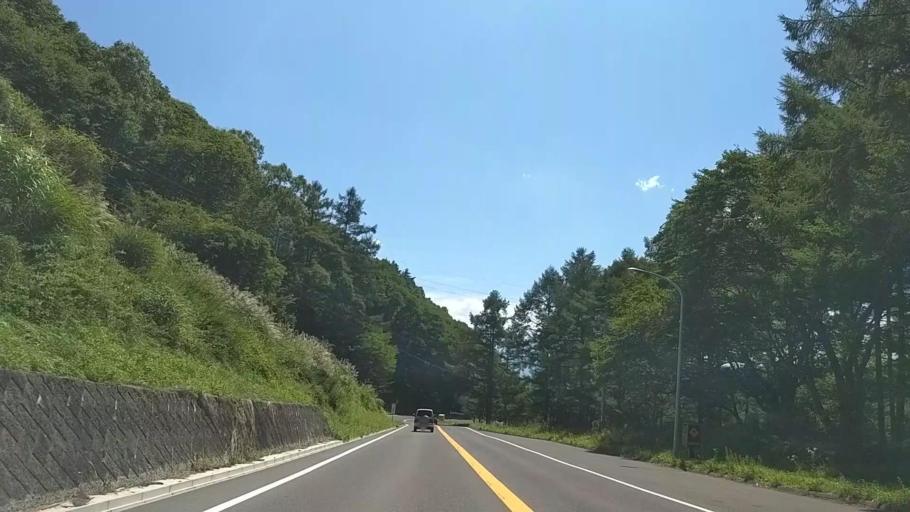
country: JP
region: Nagano
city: Chino
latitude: 36.0832
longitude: 138.2219
